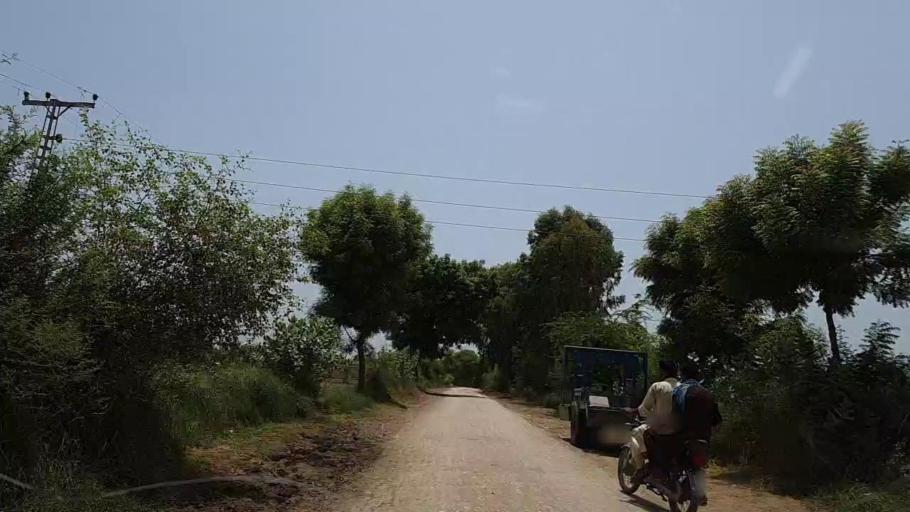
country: PK
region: Sindh
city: Tharu Shah
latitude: 26.9702
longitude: 68.0388
